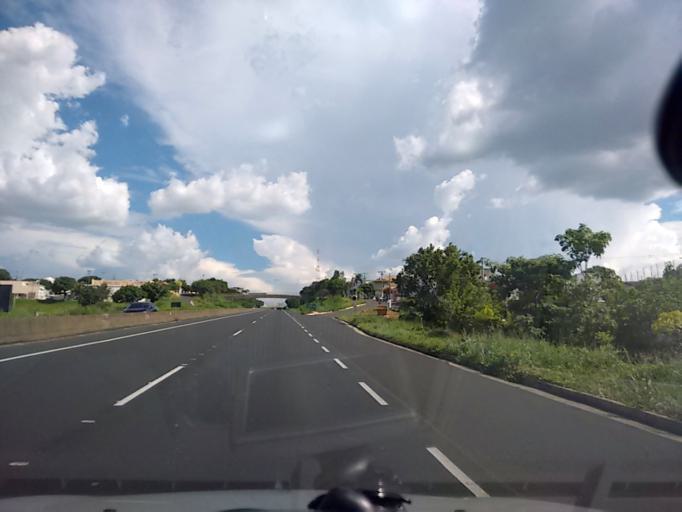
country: BR
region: Sao Paulo
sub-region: Marilia
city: Marilia
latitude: -22.2010
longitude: -49.9647
